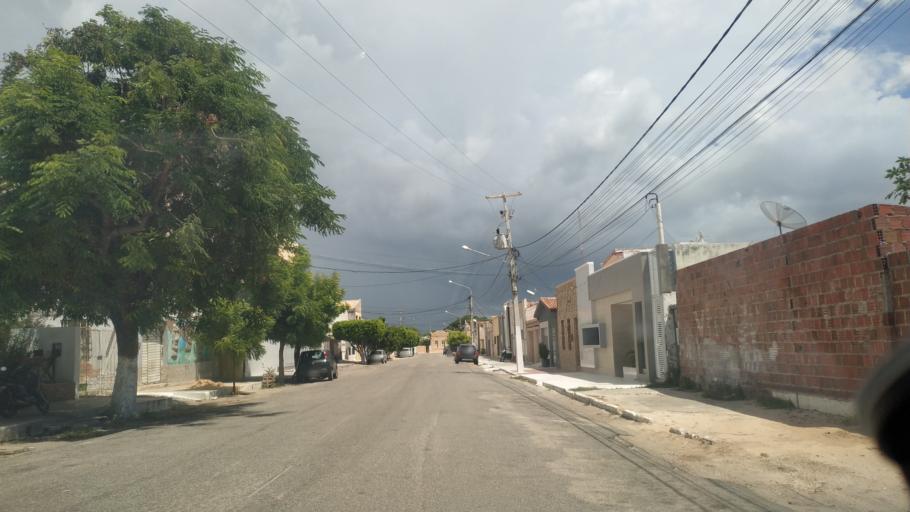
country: BR
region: Rio Grande do Norte
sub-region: Areia Branca
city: Areia Branca
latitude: -4.9567
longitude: -37.1360
